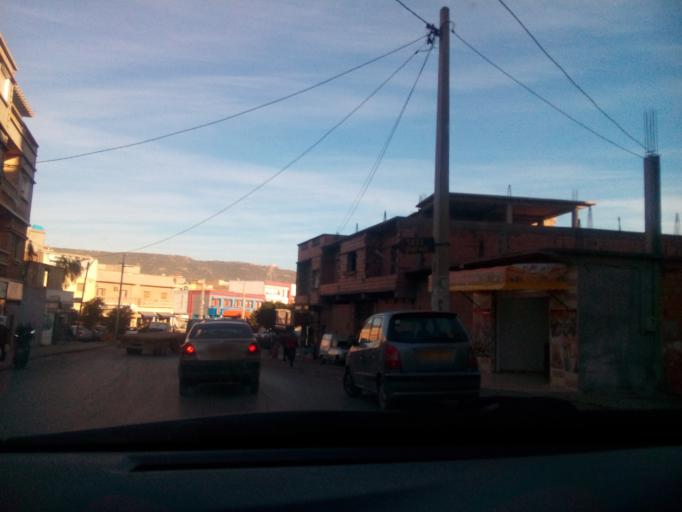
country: DZ
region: Oran
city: Oran
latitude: 35.6740
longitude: -0.6625
